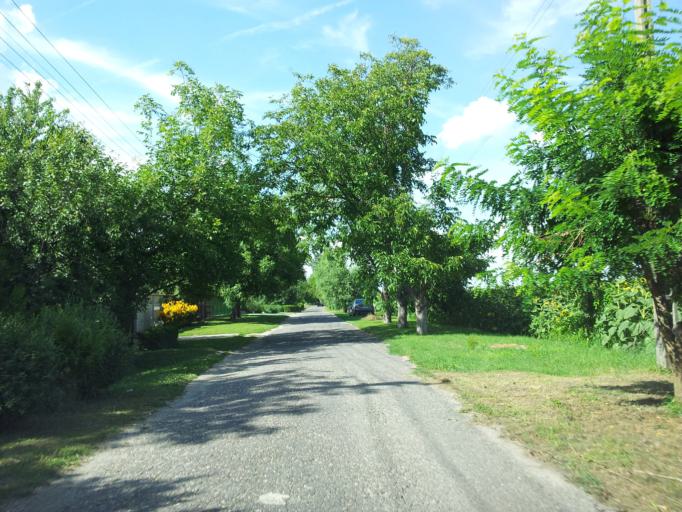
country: HU
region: Pest
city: Szigetcsep
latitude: 47.2443
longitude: 18.9787
